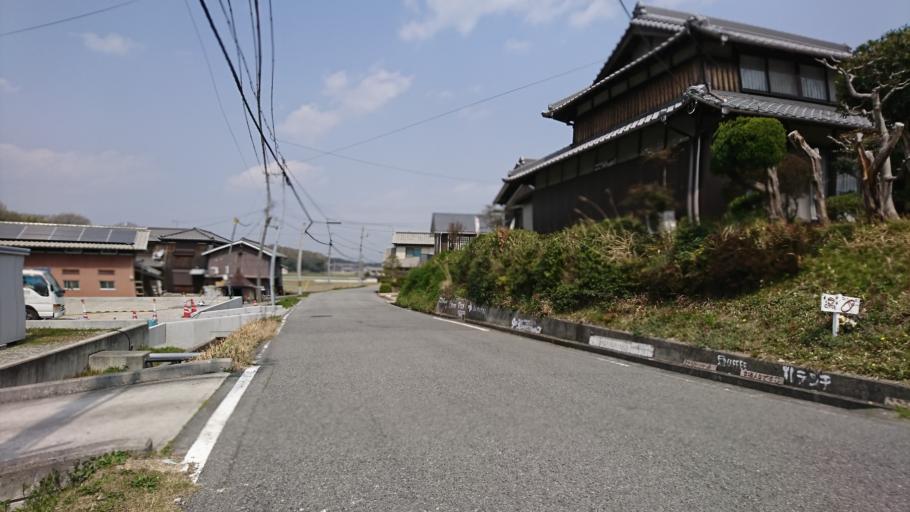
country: JP
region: Hyogo
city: Ono
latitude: 34.8321
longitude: 134.9041
